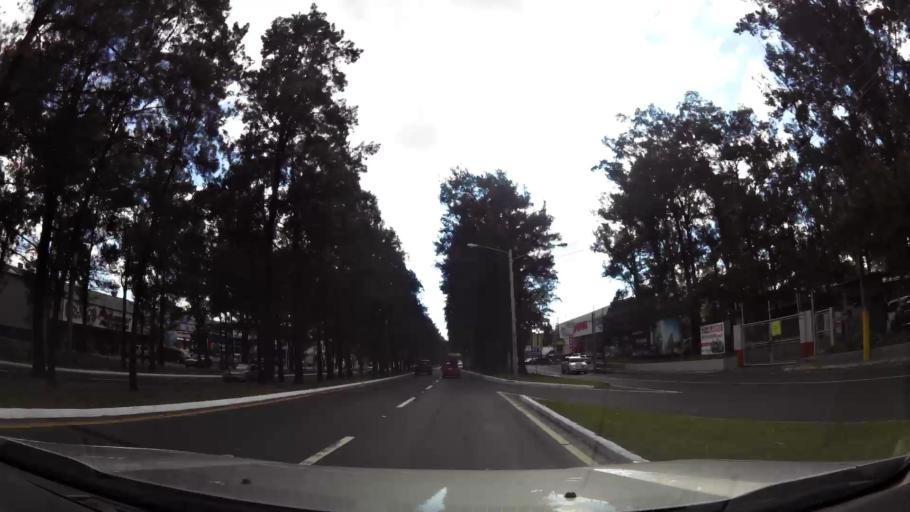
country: GT
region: Guatemala
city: Guatemala City
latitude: 14.6090
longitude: -90.5572
